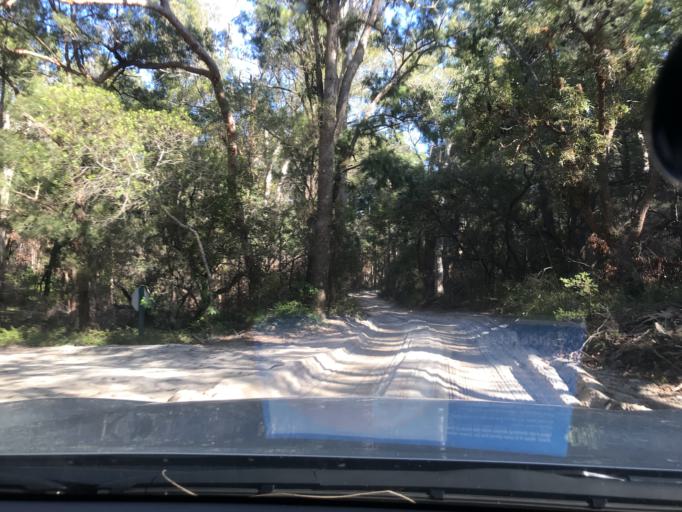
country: AU
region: Queensland
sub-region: Fraser Coast
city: Urangan
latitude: -25.5004
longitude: 153.1027
